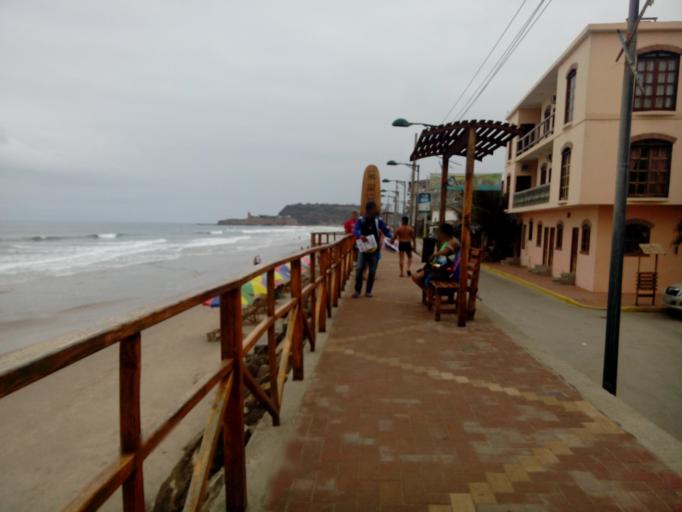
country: EC
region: Santa Elena
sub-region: Canton Santa Elena
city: Santa Elena
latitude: -1.8292
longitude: -80.7533
